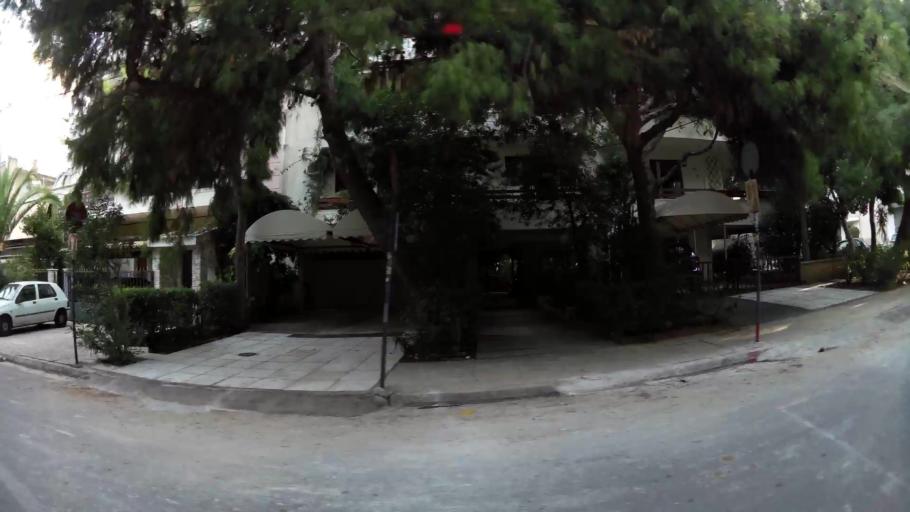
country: GR
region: Attica
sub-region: Nomarchia Athinas
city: Palaio Faliro
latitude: 37.9344
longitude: 23.7088
